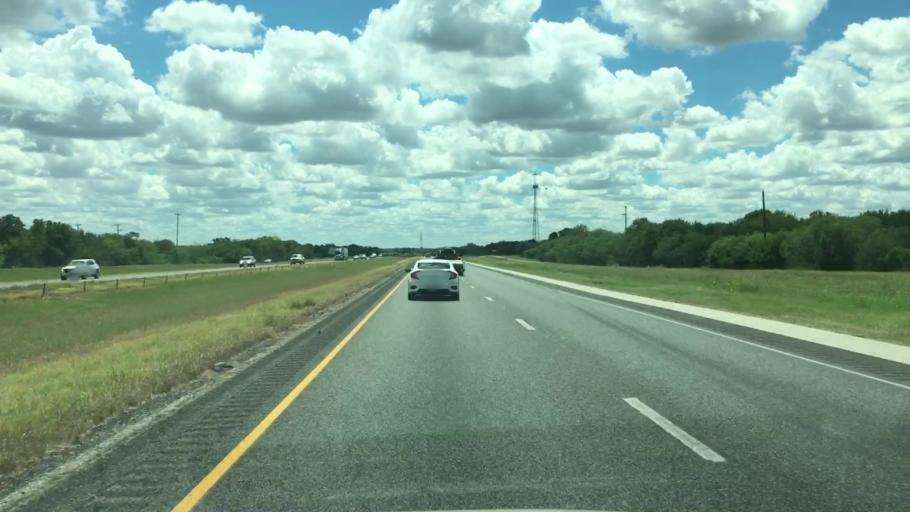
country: US
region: Texas
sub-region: Bexar County
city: Elmendorf
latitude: 29.2646
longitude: -98.3958
